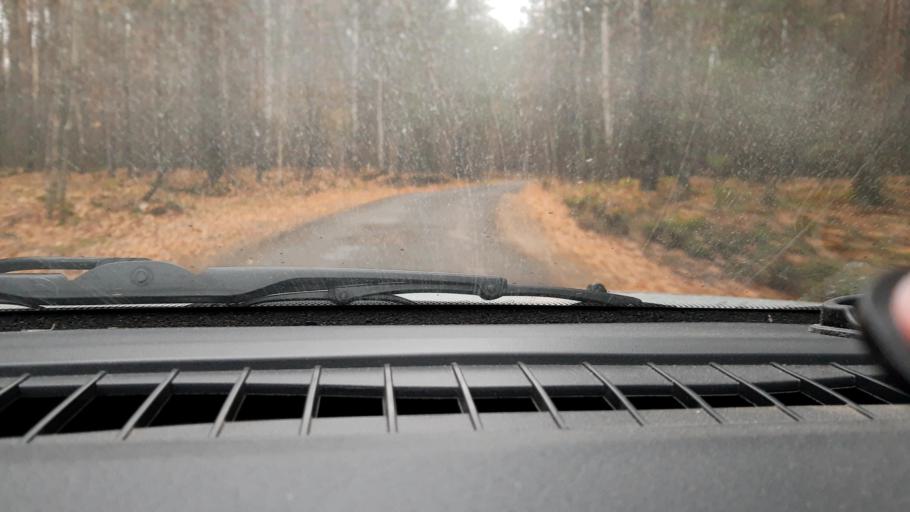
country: RU
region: Nizjnij Novgorod
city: Sitniki
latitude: 56.4210
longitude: 44.0470
